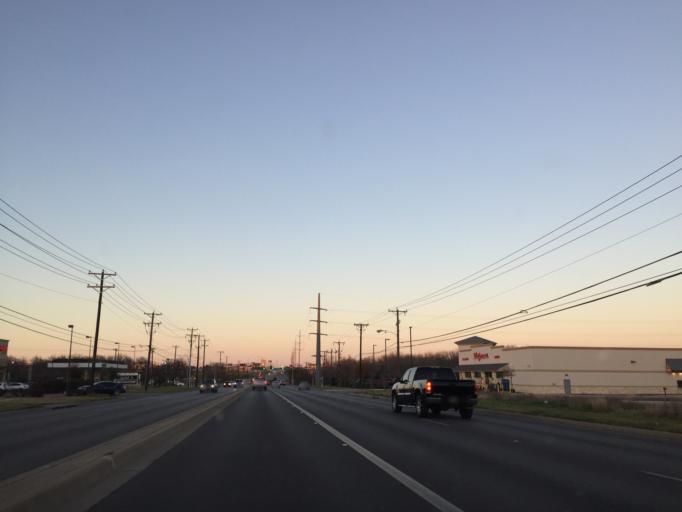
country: US
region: Texas
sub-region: Travis County
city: Pflugerville
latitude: 30.4542
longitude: -97.6030
